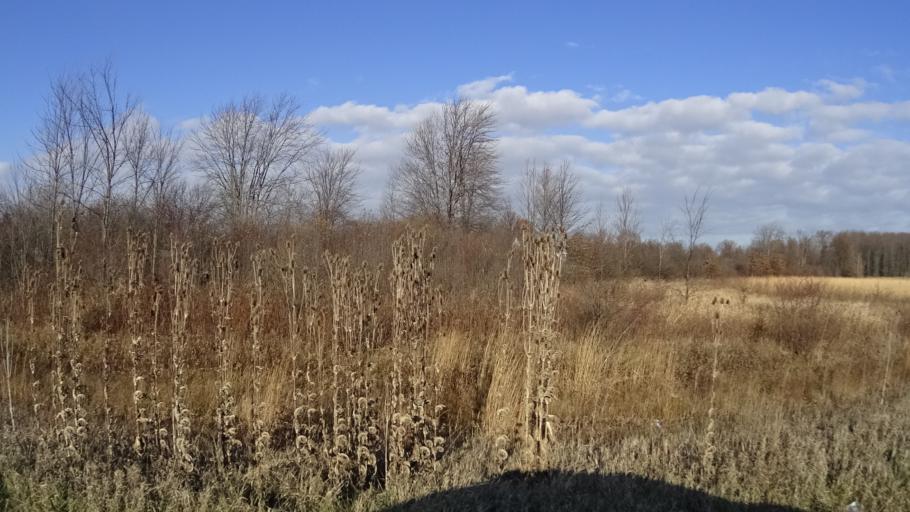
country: US
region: Ohio
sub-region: Lorain County
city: Oberlin
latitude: 41.2824
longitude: -82.1869
